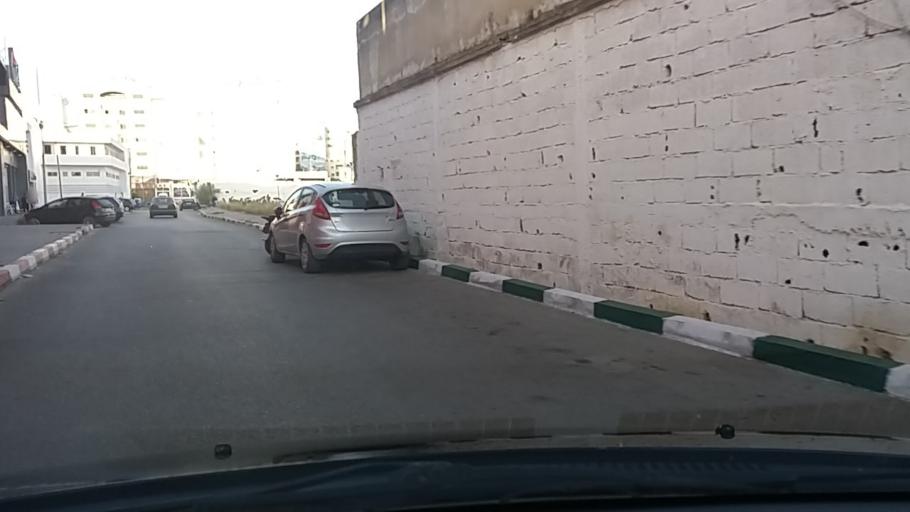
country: MA
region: Gharb-Chrarda-Beni Hssen
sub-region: Kenitra Province
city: Kenitra
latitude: 34.2551
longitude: -6.5987
